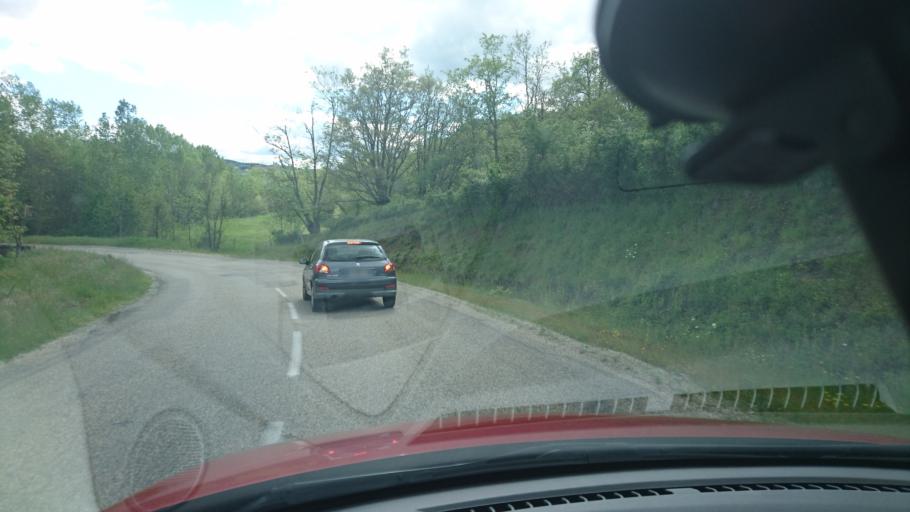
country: FR
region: Rhone-Alpes
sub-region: Departement de la Loire
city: Maclas
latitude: 45.3427
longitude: 4.6878
